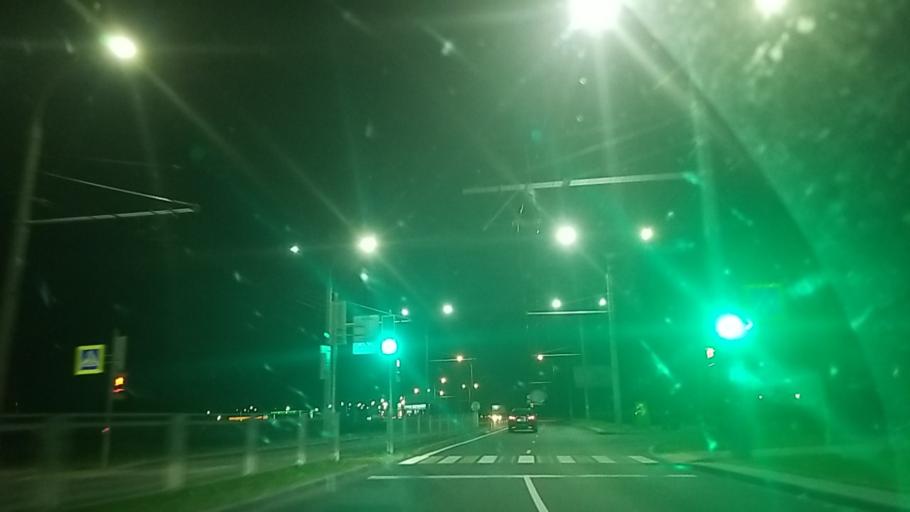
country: BY
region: Brest
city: Brest
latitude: 52.0775
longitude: 23.7688
